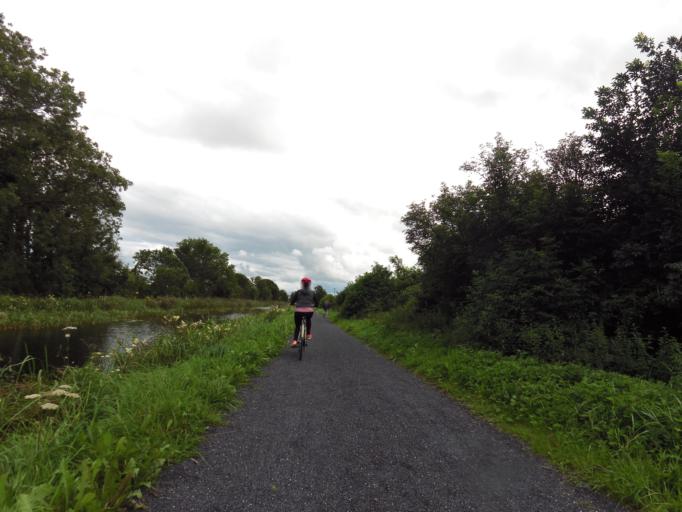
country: IE
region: Leinster
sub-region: An Iarmhi
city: An Muileann gCearr
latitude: 53.5491
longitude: -7.4764
